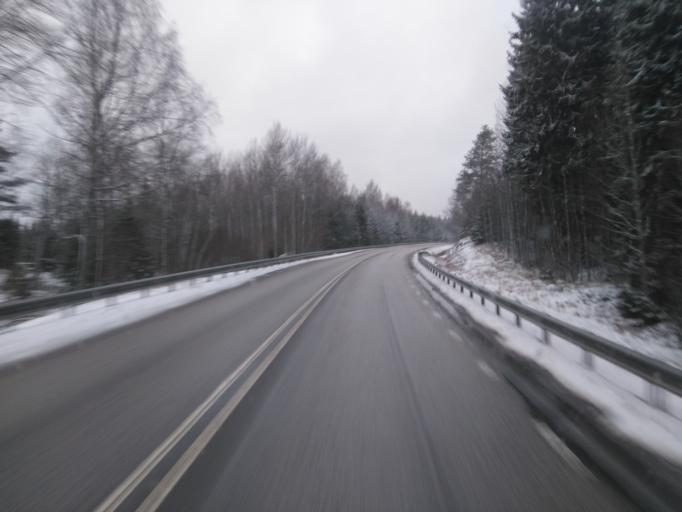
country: SE
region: Joenkoeping
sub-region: Eksjo Kommun
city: Eksjoe
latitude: 57.6442
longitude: 15.0634
